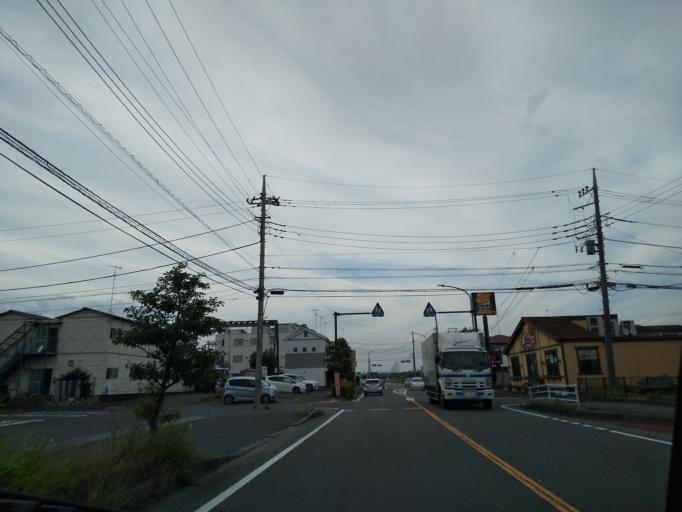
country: JP
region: Kanagawa
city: Atsugi
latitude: 35.4683
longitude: 139.3591
